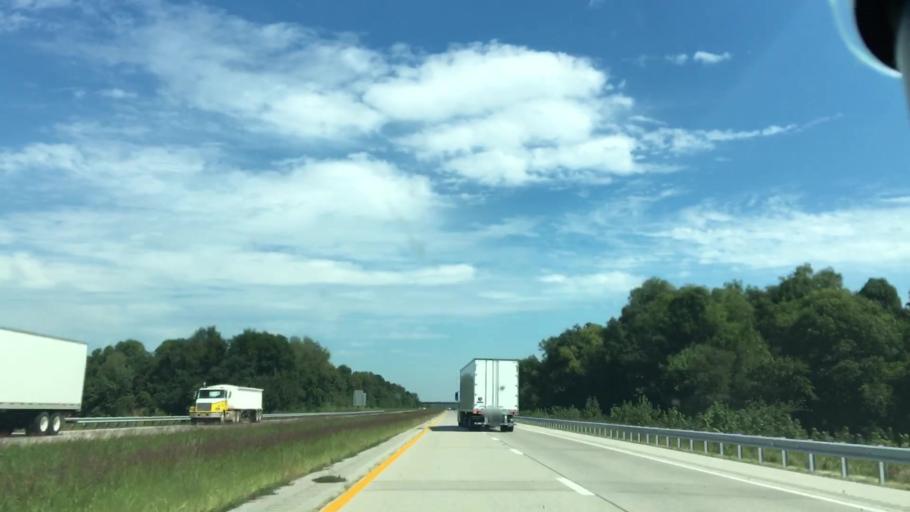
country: US
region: Kentucky
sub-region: Daviess County
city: Owensboro
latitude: 37.7603
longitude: -87.2427
